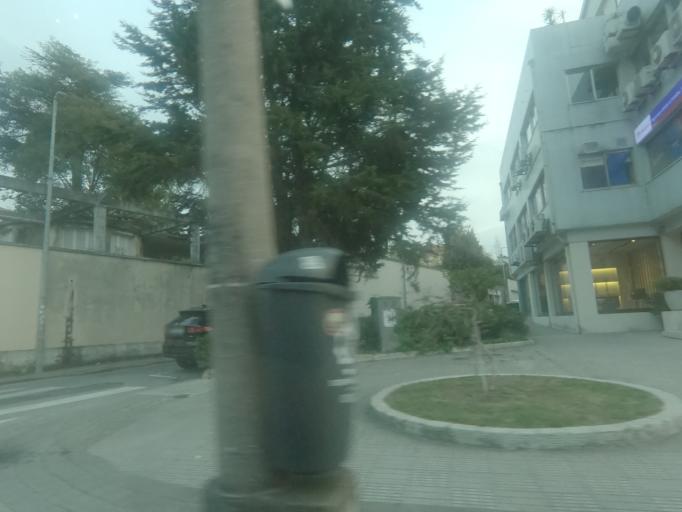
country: PT
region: Porto
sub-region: Matosinhos
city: Senhora da Hora
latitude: 41.1624
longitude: -8.6573
